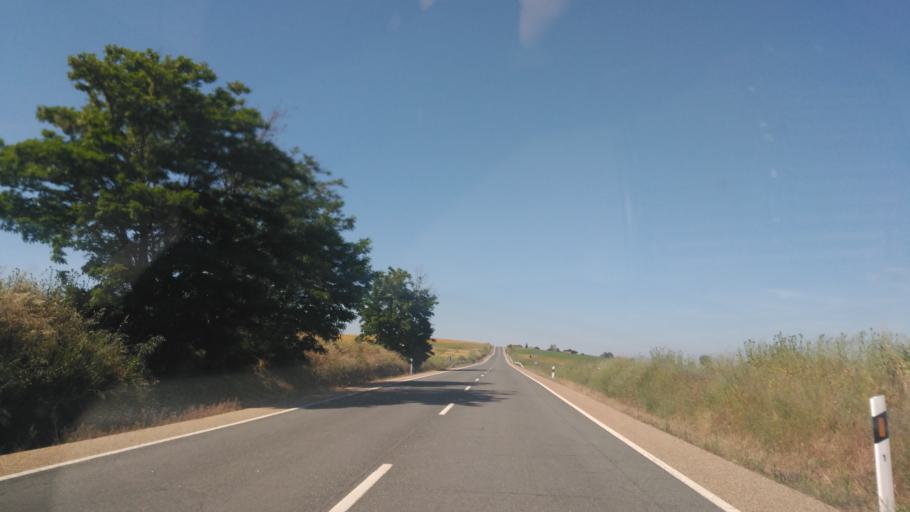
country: ES
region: Castille and Leon
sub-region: Provincia de Zamora
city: Corrales
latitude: 41.3307
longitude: -5.7329
